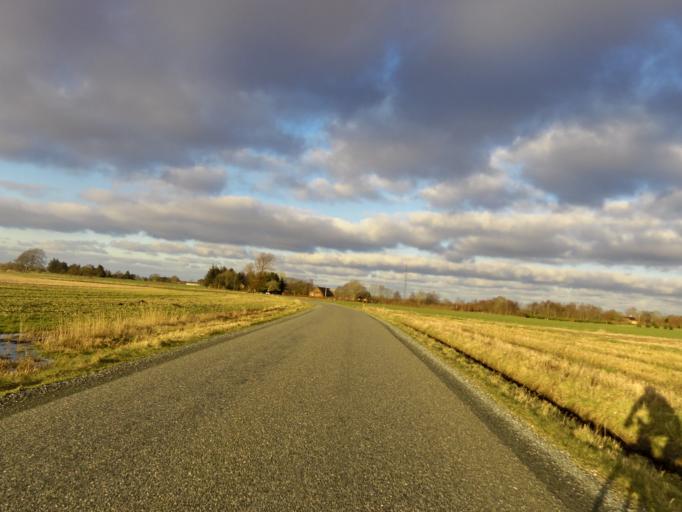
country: DK
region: South Denmark
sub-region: Esbjerg Kommune
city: Ribe
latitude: 55.2882
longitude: 8.8469
